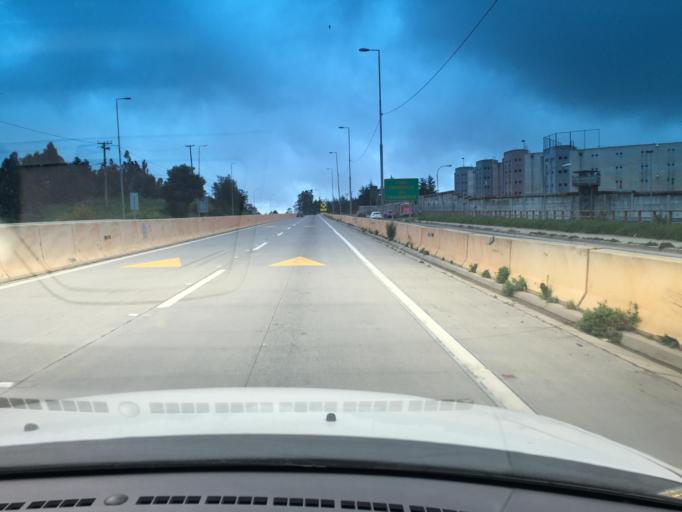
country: CL
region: Valparaiso
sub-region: Provincia de Valparaiso
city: Valparaiso
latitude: -33.0684
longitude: -71.6319
